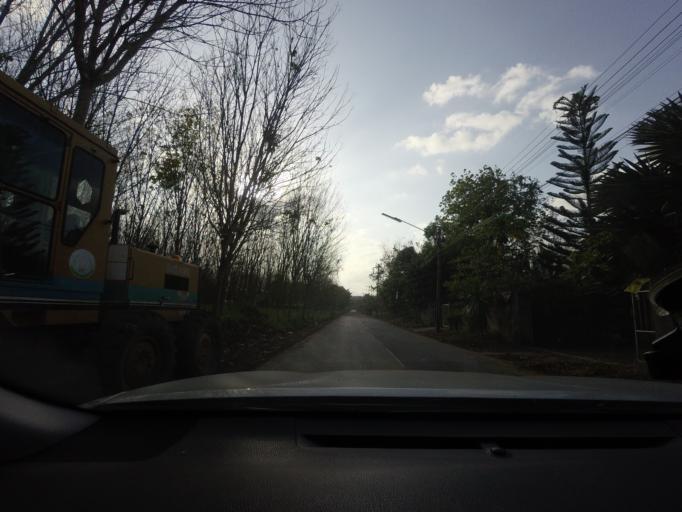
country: TH
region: Pattani
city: Mae Lan
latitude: 6.6155
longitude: 101.2422
